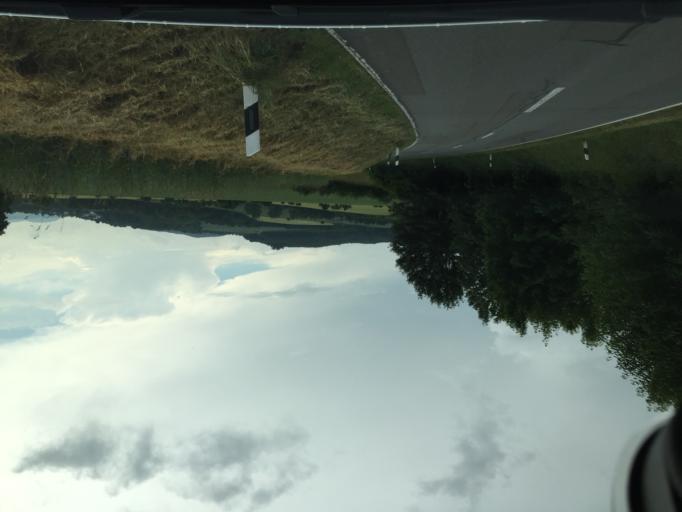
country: DE
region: Lower Saxony
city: Vahlbruch
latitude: 51.9979
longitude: 9.3479
